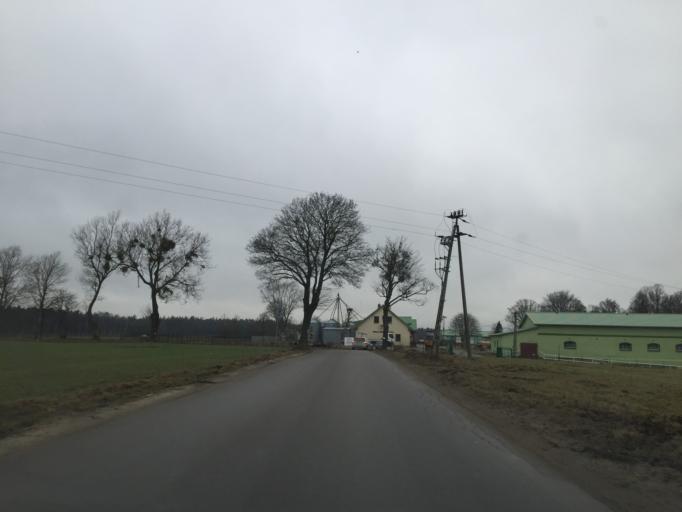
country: PL
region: Pomeranian Voivodeship
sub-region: Powiat kartuski
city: Banino
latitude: 54.4041
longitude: 18.4325
